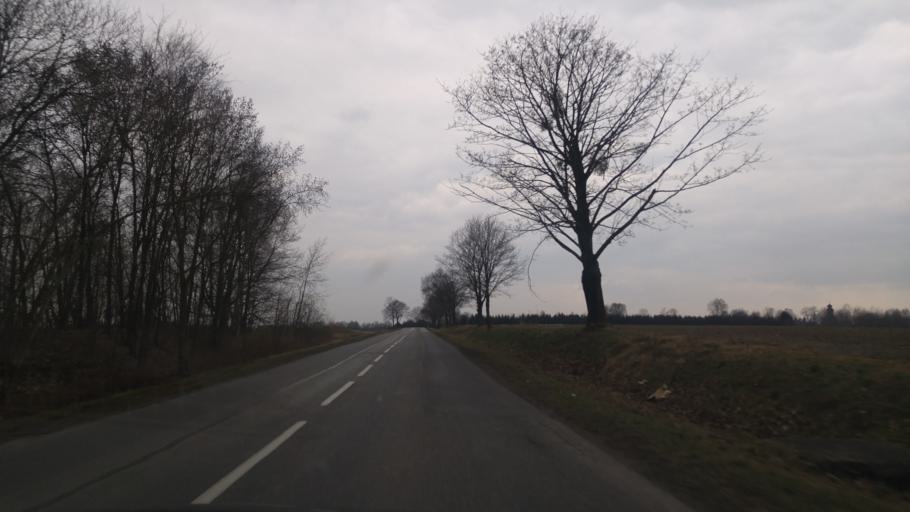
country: PL
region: Silesian Voivodeship
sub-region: Powiat cieszynski
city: Chybie
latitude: 49.9354
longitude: 18.8081
